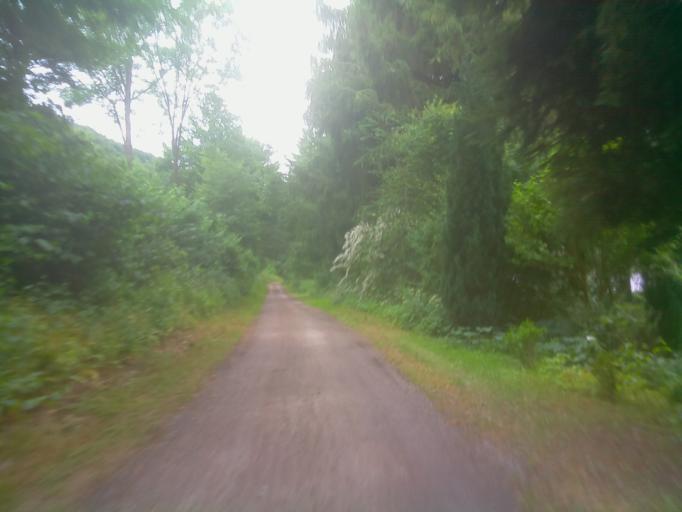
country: DE
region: Hesse
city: Neckarsteinach
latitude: 49.4050
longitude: 8.8674
